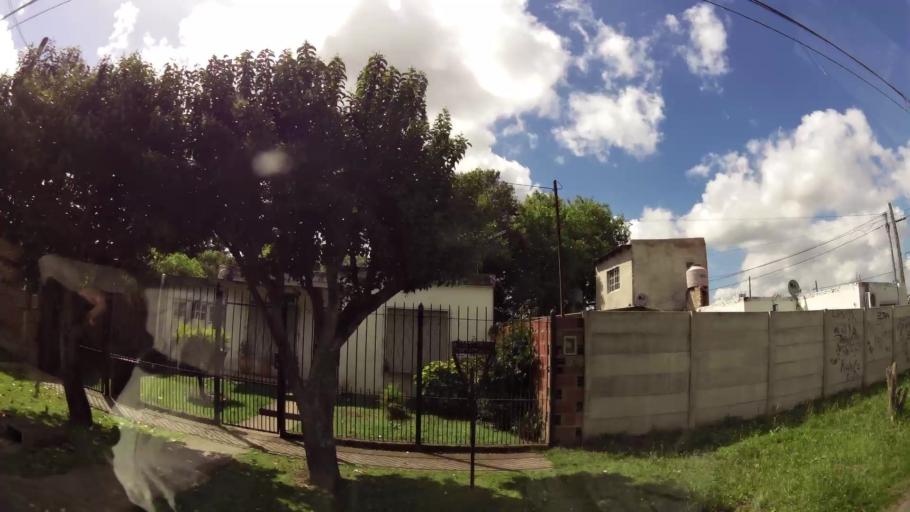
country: AR
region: Buenos Aires
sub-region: Partido de Quilmes
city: Quilmes
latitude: -34.8262
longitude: -58.1899
